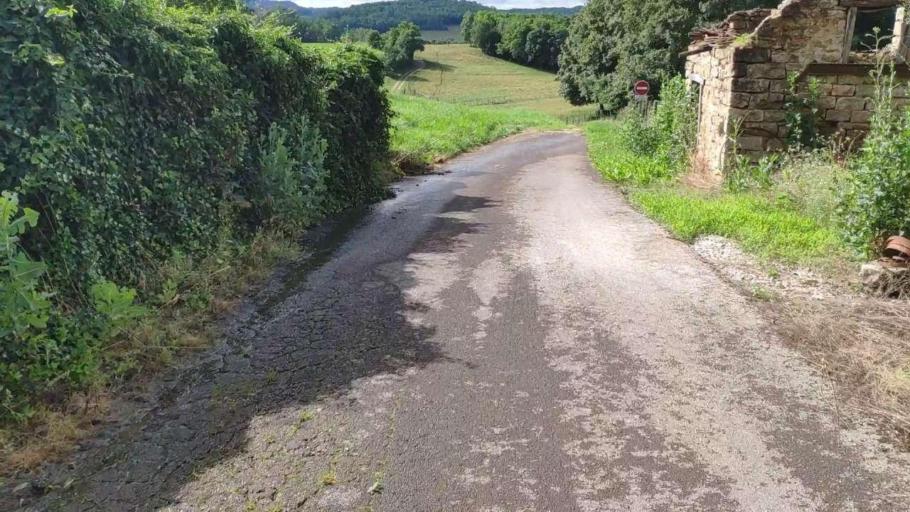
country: FR
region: Franche-Comte
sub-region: Departement du Jura
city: Poligny
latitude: 46.8217
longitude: 5.5876
